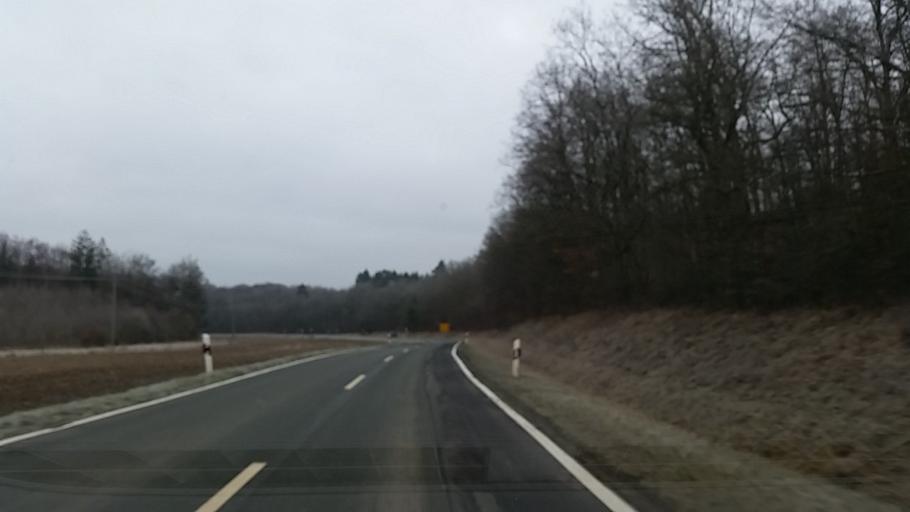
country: DE
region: Bavaria
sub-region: Regierungsbezirk Unterfranken
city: Fuchsstadt
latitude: 50.0763
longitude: 9.9154
